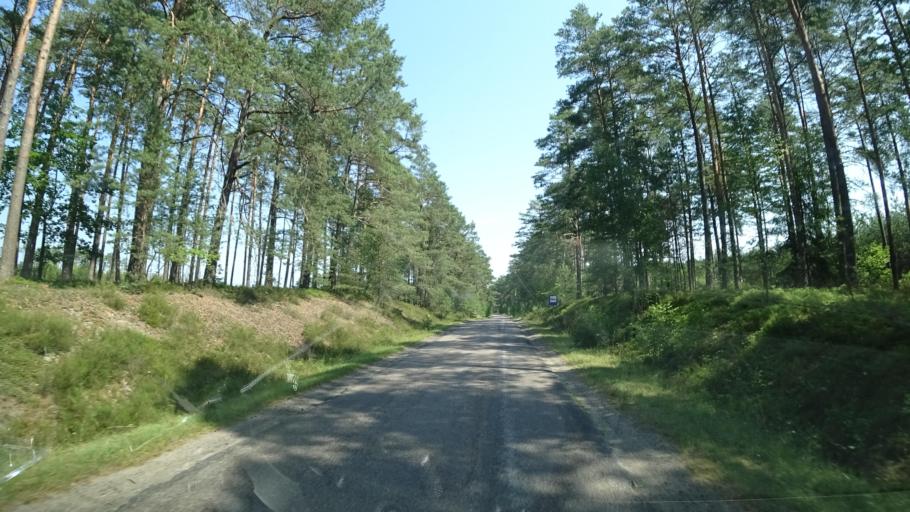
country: PL
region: Pomeranian Voivodeship
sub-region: Powiat chojnicki
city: Brusy
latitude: 53.8672
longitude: 17.6154
